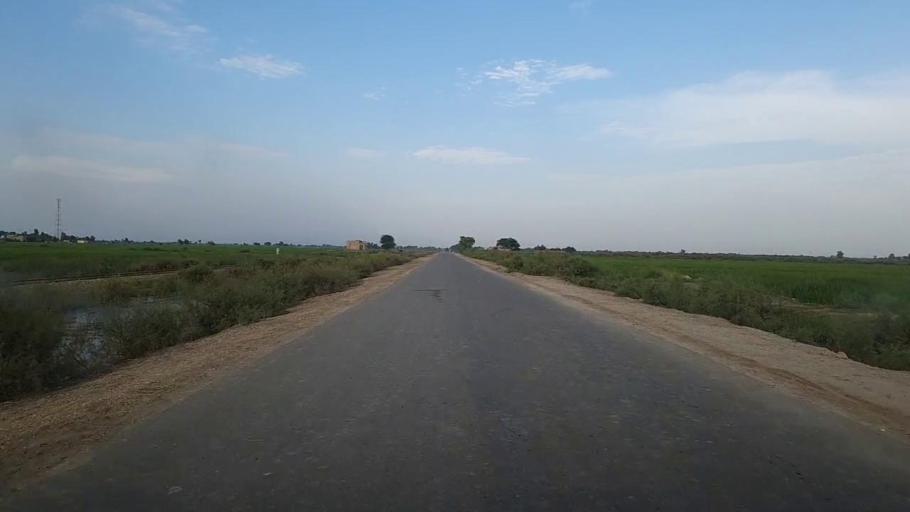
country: PK
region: Sindh
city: Thul
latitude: 28.2823
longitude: 68.8568
